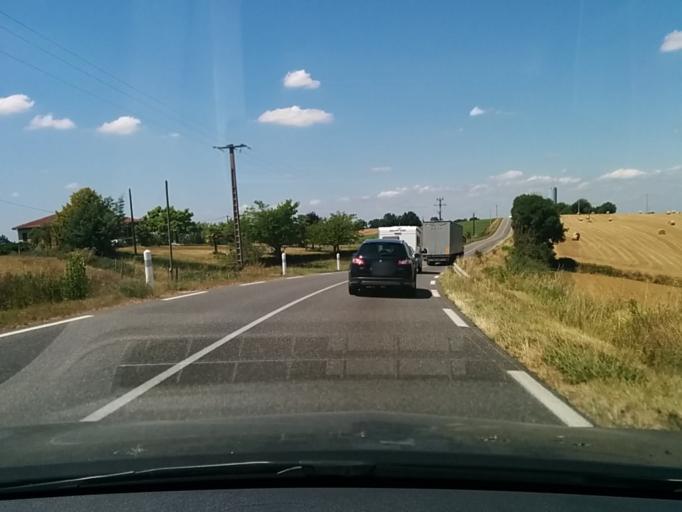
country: FR
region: Midi-Pyrenees
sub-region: Departement du Gers
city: Eauze
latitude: 43.7737
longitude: 0.1252
